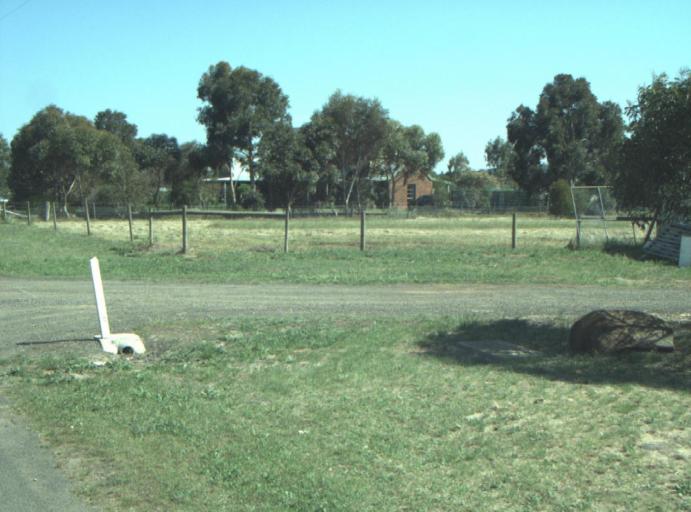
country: AU
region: Victoria
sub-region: Greater Geelong
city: Lara
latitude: -38.0198
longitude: 144.3568
